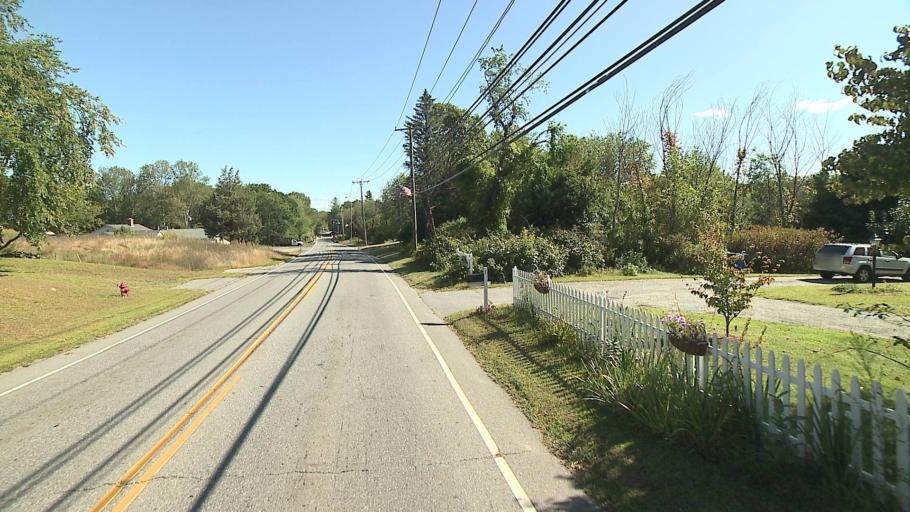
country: US
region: Connecticut
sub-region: Windham County
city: Plainfield Village
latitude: 41.6623
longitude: -71.9221
